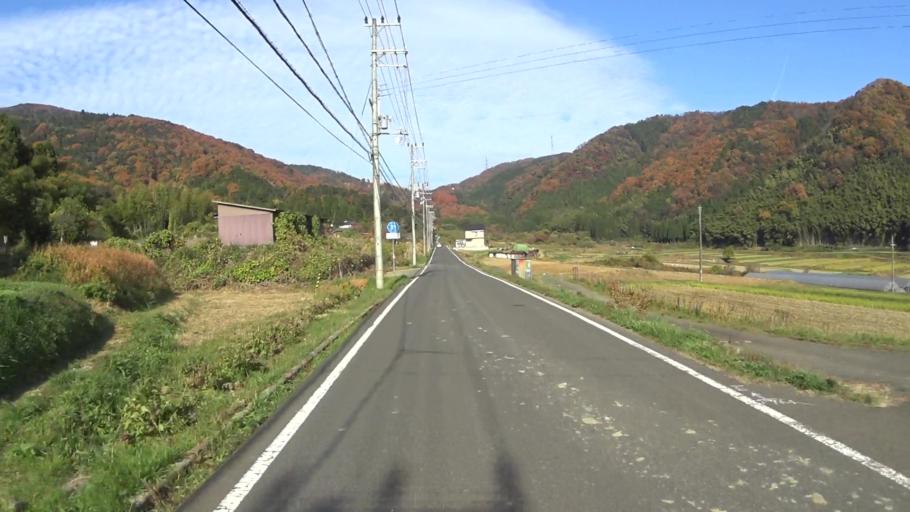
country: JP
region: Kyoto
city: Maizuru
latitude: 35.5228
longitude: 135.3901
